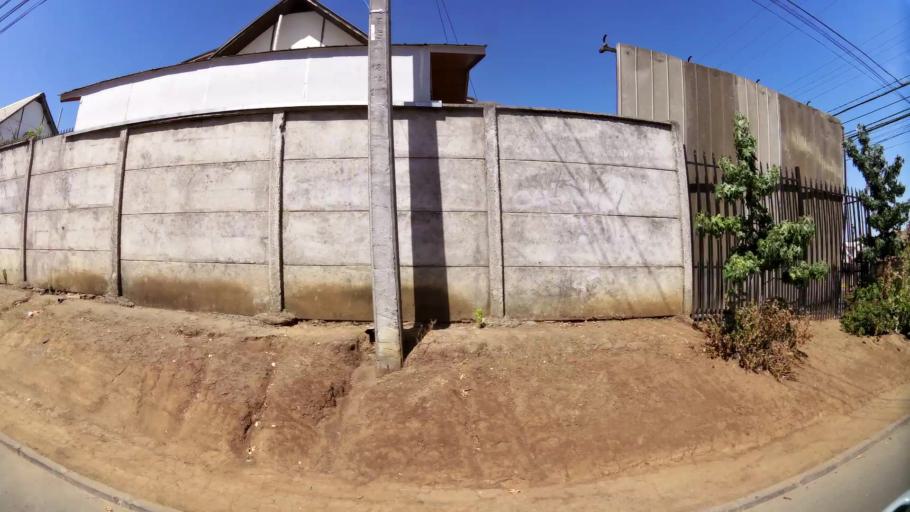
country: CL
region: Maule
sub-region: Provincia de Talca
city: Talca
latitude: -35.4265
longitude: -71.6253
